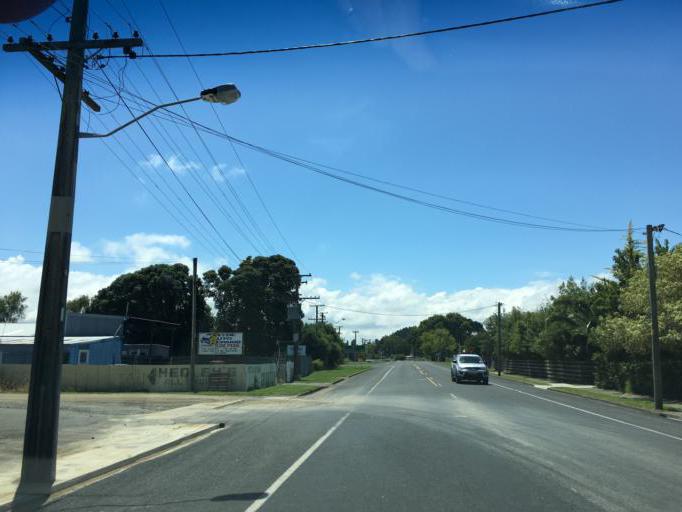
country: NZ
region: Hawke's Bay
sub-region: Wairoa District
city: Wairoa
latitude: -39.0256
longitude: 177.4175
